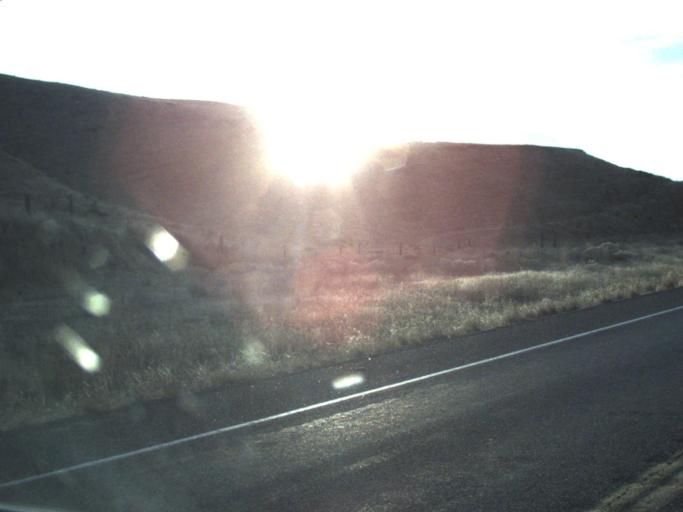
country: US
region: Washington
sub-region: Benton County
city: Finley
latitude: 46.0726
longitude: -118.7952
